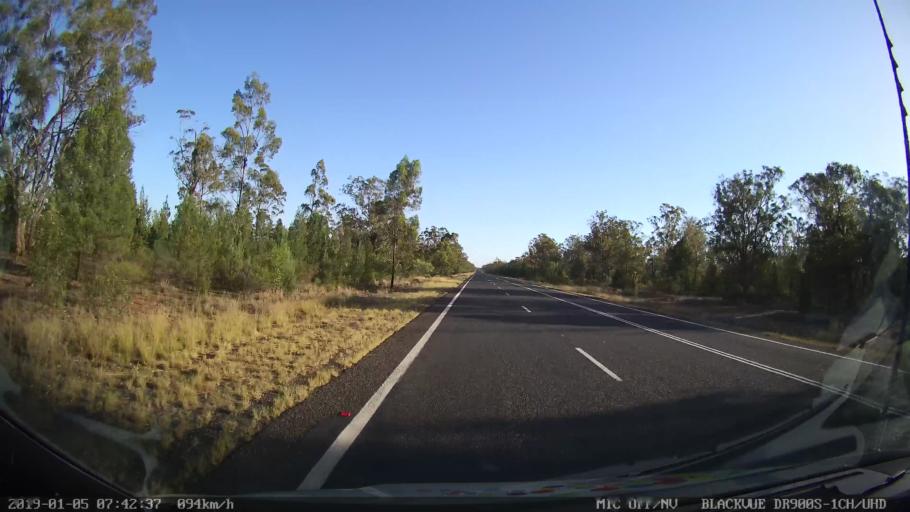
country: AU
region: New South Wales
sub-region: Gilgandra
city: Gilgandra
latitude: -31.8956
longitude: 148.6282
